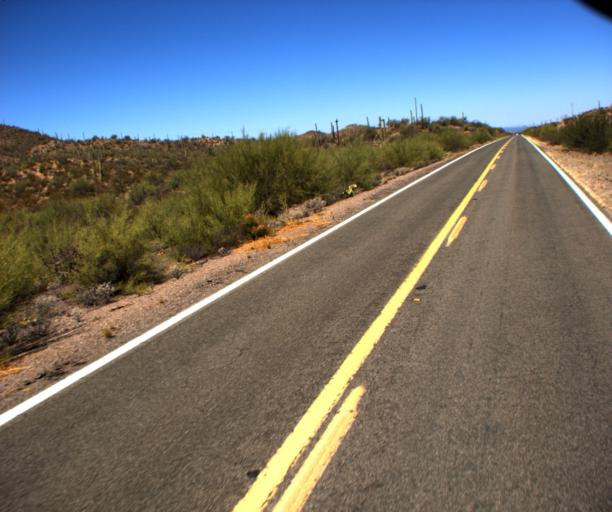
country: US
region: Arizona
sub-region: Pima County
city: Sells
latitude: 32.1742
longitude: -112.1716
